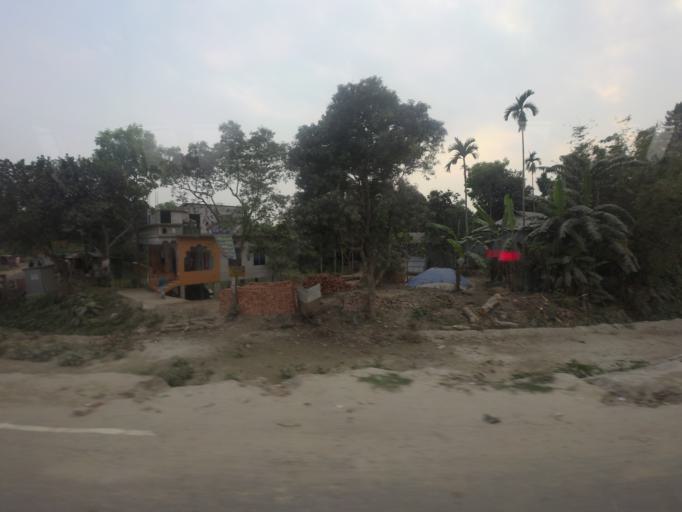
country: BD
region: Dhaka
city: Tangail
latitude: 24.1872
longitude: 89.9963
